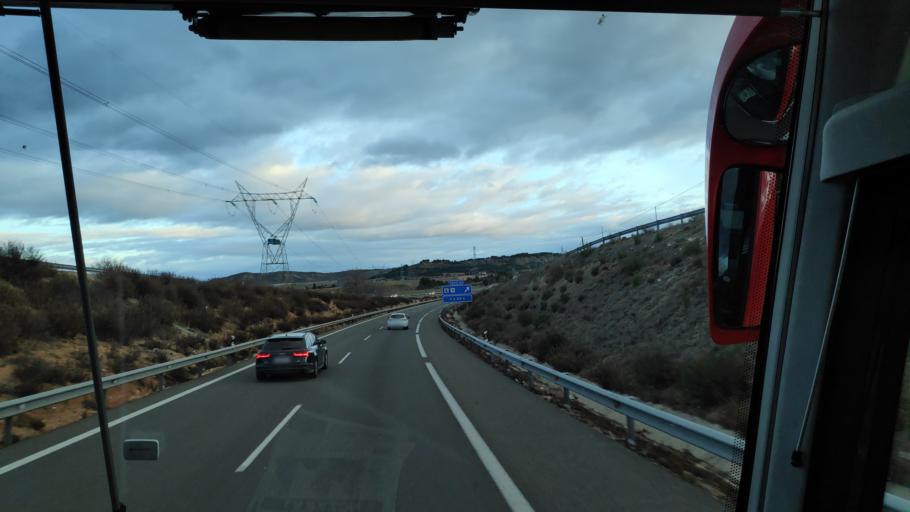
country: ES
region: Castille-La Mancha
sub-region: Provincia de Cuenca
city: Belinchon
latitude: 40.0424
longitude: -3.0557
